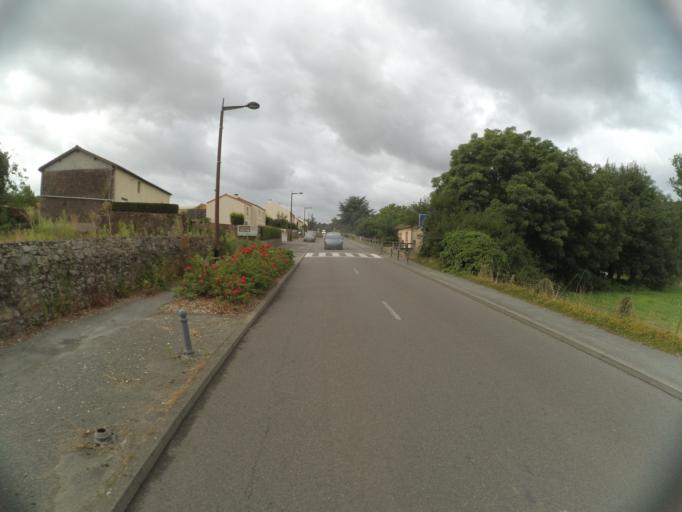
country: FR
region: Pays de la Loire
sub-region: Departement de Maine-et-Loire
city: Montfaucon-Montigne
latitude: 47.0962
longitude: -1.1269
